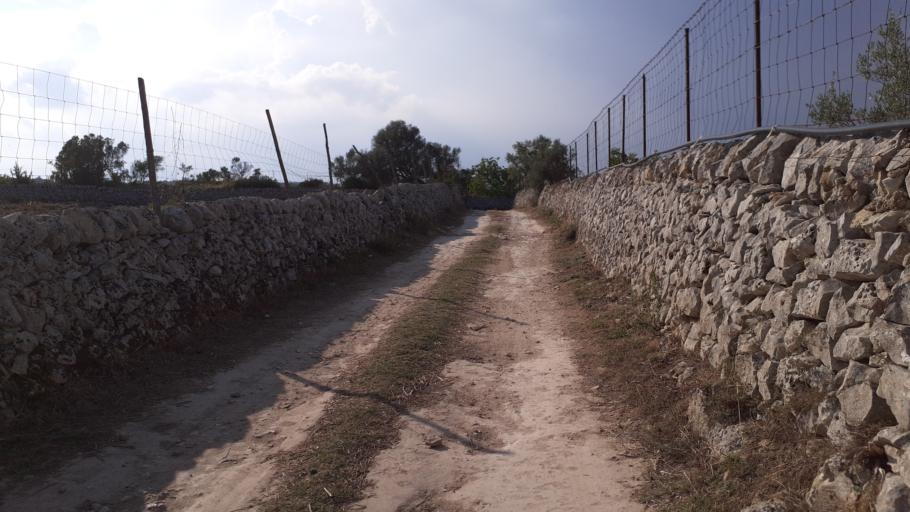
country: IT
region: Sicily
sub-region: Provincia di Siracusa
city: Canicattini Bagni
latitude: 36.9805
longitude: 15.0926
